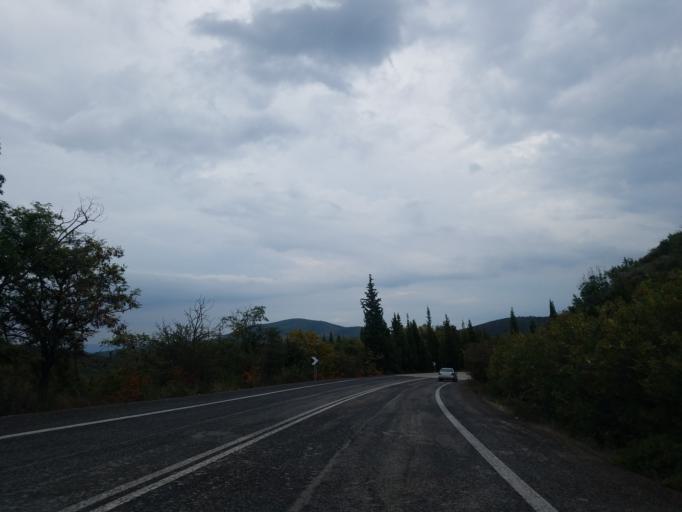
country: GR
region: Central Greece
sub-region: Nomos Voiotias
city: Stirion
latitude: 38.4499
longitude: 22.7857
